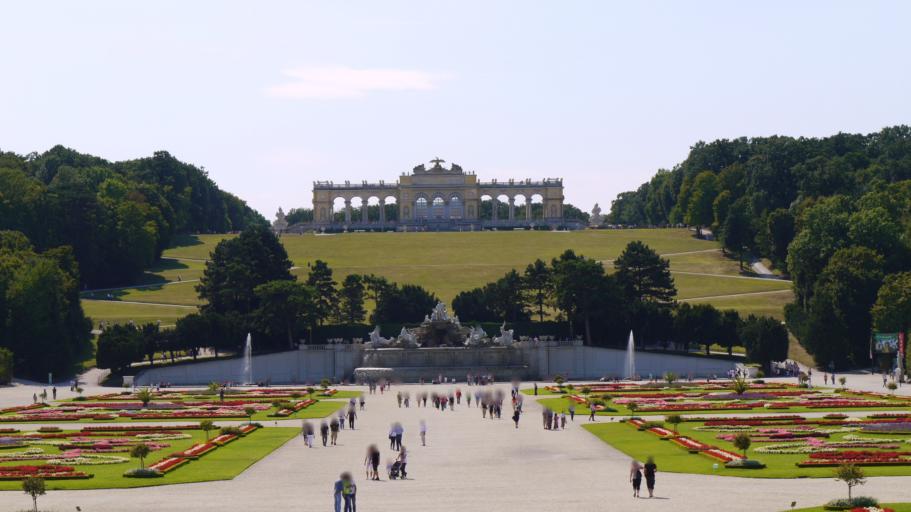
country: AT
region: Vienna
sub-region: Wien Stadt
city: Vienna
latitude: 48.1848
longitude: 16.3121
